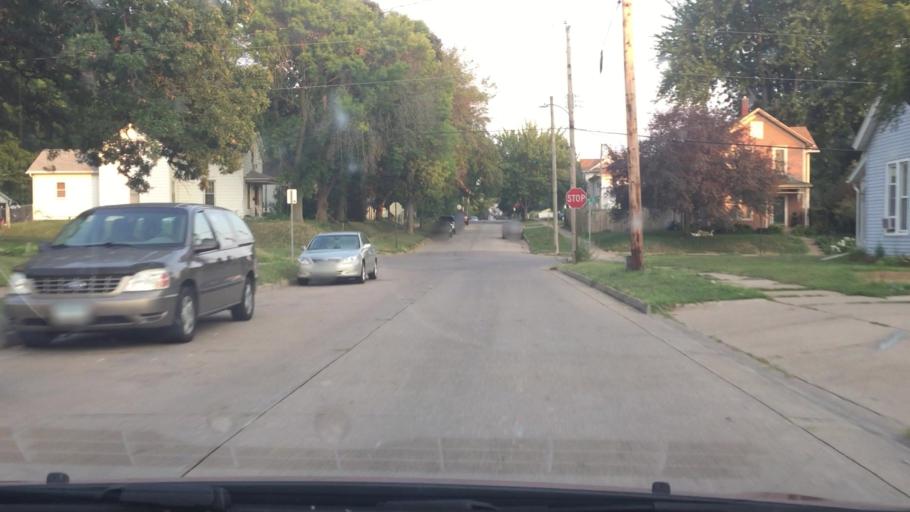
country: US
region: Iowa
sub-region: Muscatine County
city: Muscatine
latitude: 41.4323
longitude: -91.0468
